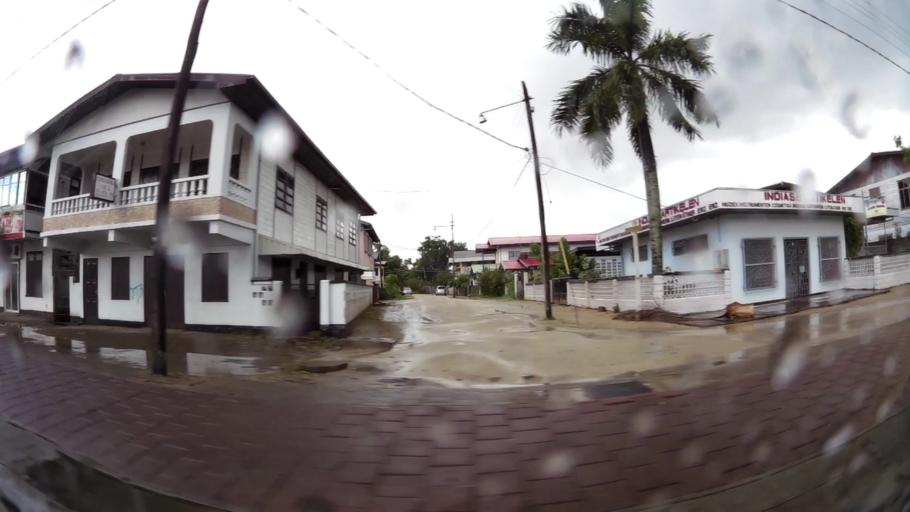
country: SR
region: Paramaribo
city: Paramaribo
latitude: 5.8234
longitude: -55.1721
